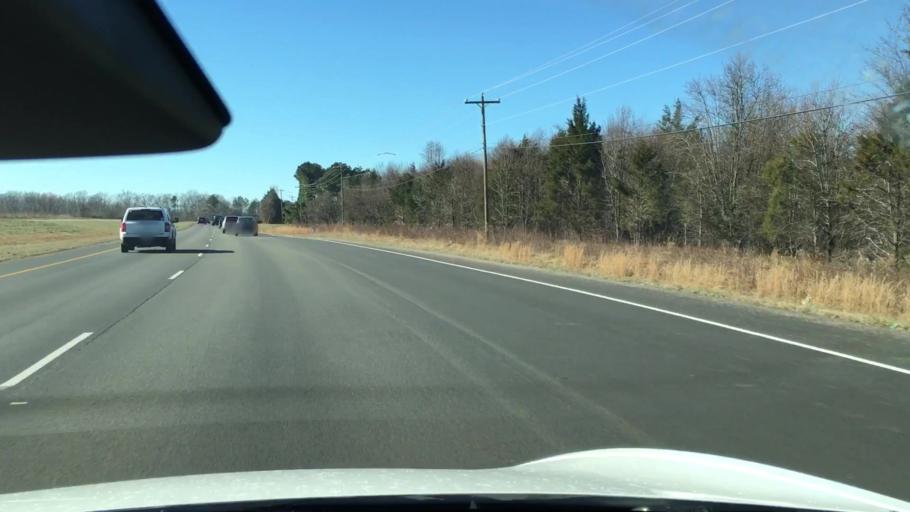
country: US
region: Virginia
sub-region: Chesterfield County
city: Woodlake
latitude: 37.5103
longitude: -77.7006
